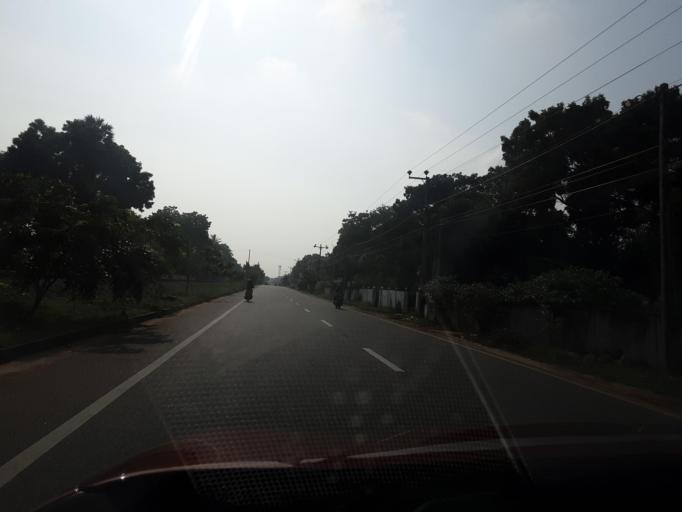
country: LK
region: Northern Province
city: Valvedditturai
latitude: 9.6633
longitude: 80.1710
